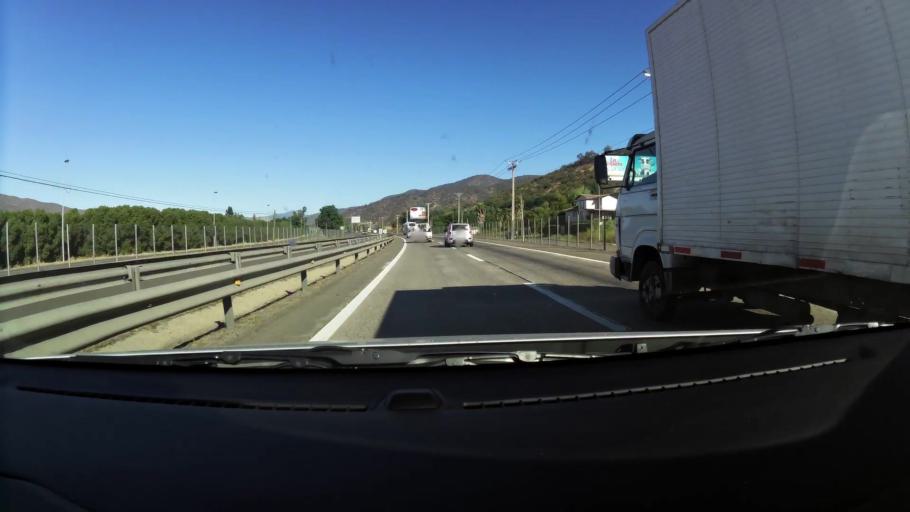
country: CL
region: Santiago Metropolitan
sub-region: Provincia de Chacabuco
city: Lampa
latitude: -33.4117
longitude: -71.0575
